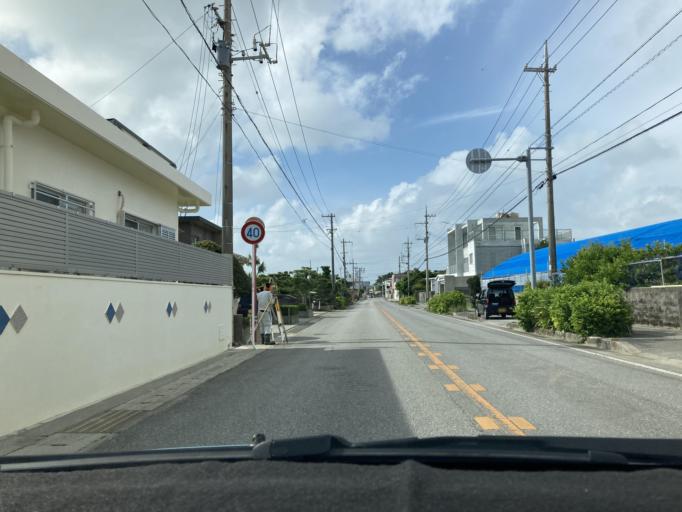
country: JP
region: Okinawa
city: Itoman
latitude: 26.1035
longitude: 127.6687
